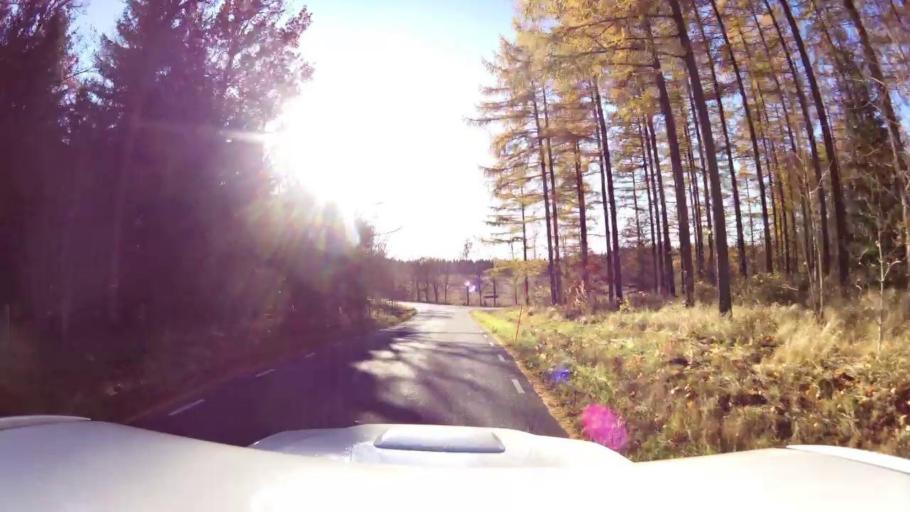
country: SE
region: OEstergoetland
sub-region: Linkopings Kommun
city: Sturefors
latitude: 58.2553
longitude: 15.6626
